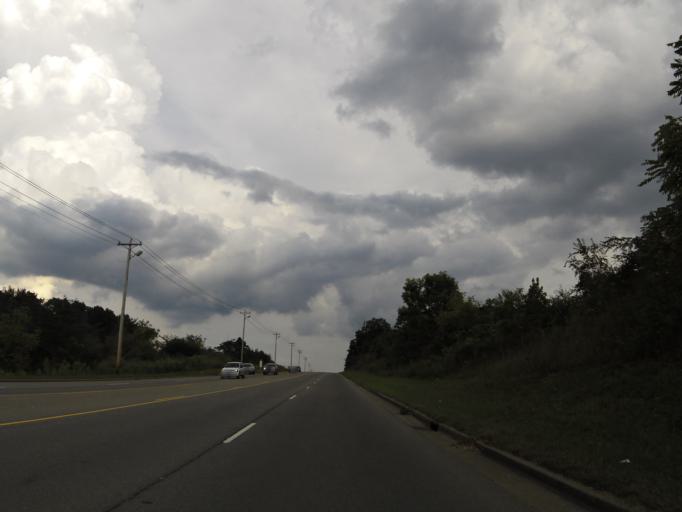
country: US
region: Tennessee
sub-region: Dickson County
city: Dickson
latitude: 36.0648
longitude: -87.3946
